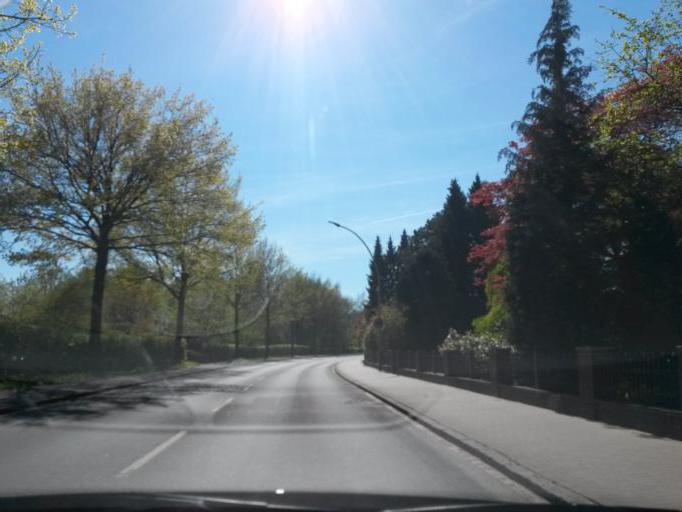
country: DE
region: Schleswig-Holstein
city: Halstenbek
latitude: 53.6265
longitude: 9.8326
